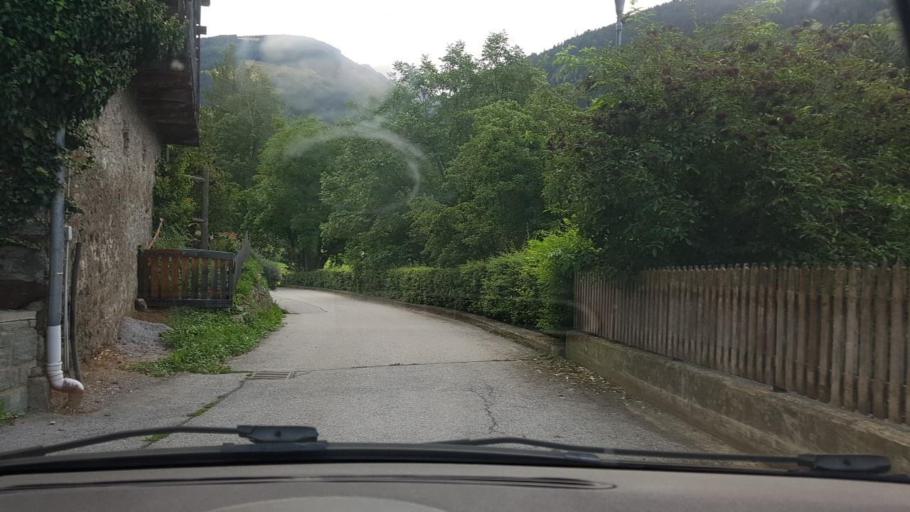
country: AT
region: Carinthia
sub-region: Politischer Bezirk Spittal an der Drau
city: Rangersdorf
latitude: 46.8606
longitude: 12.9506
